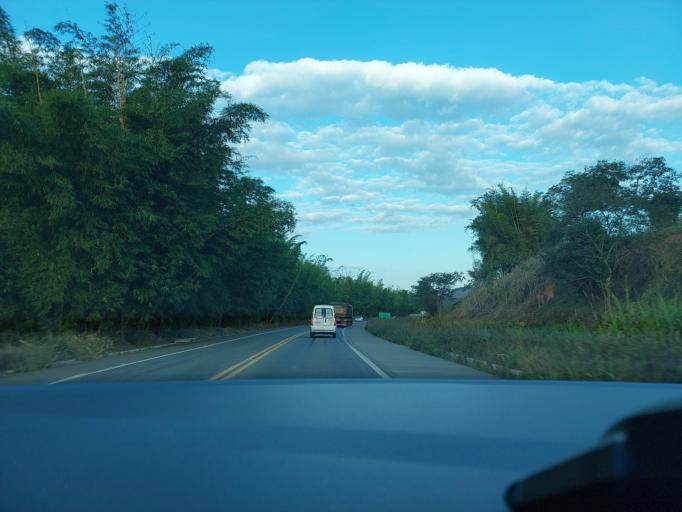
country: BR
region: Minas Gerais
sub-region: Muriae
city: Muriae
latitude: -21.1382
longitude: -42.1763
